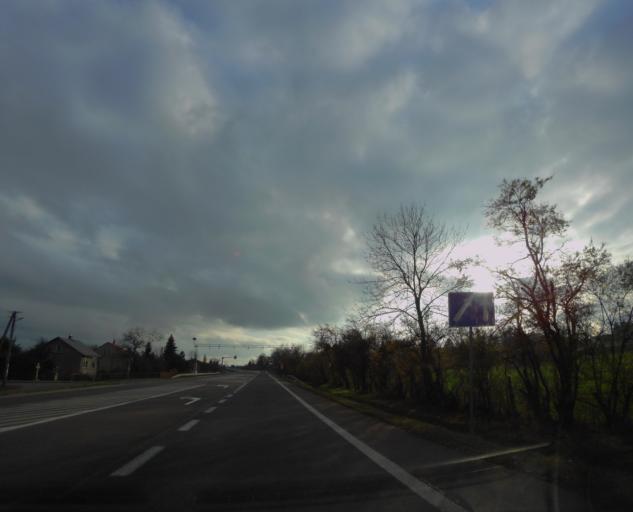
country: PL
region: Subcarpathian Voivodeship
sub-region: Powiat przemyski
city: Orly
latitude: 49.9018
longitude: 22.8169
